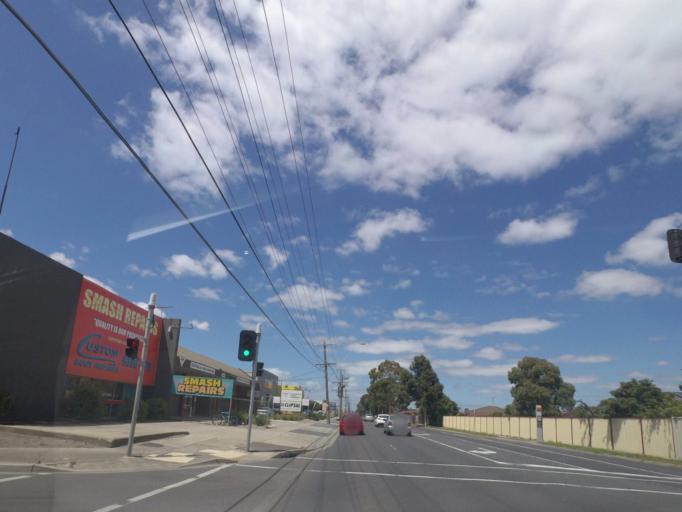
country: AU
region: Victoria
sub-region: Brimbank
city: Albion
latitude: -37.7546
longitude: 144.8329
